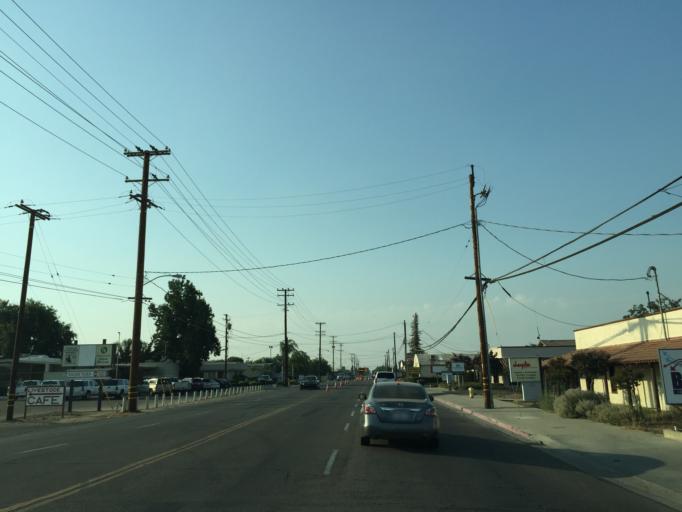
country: US
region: California
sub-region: Tulare County
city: Visalia
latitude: 36.3356
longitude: -119.2787
